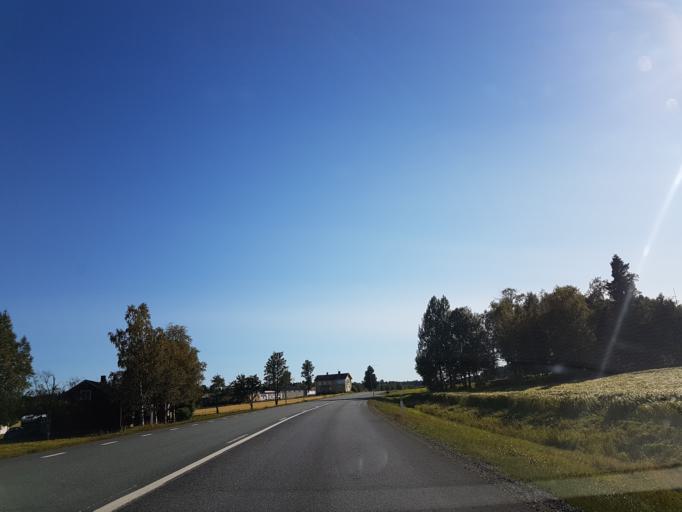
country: SE
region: Vaesterbotten
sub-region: Skelleftea Kommun
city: Burea
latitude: 64.3805
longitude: 21.3043
